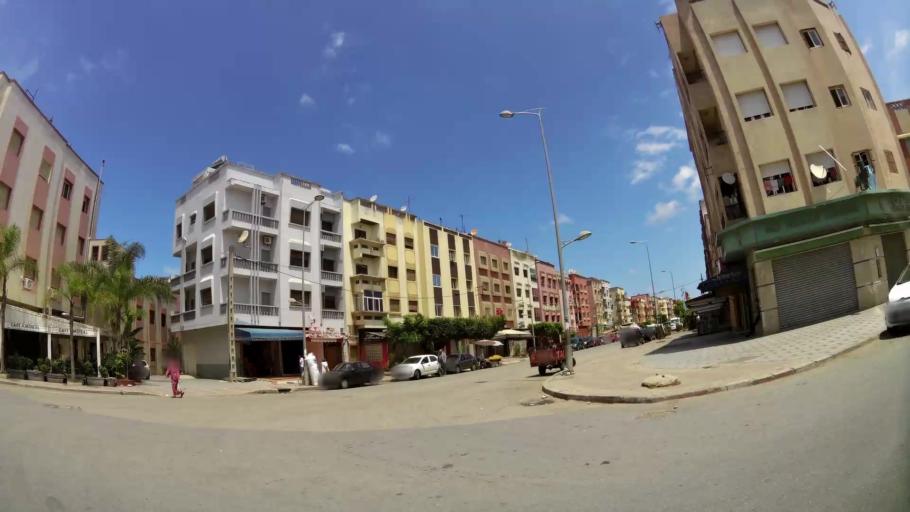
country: MA
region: Gharb-Chrarda-Beni Hssen
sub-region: Kenitra Province
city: Kenitra
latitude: 34.2677
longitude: -6.6019
